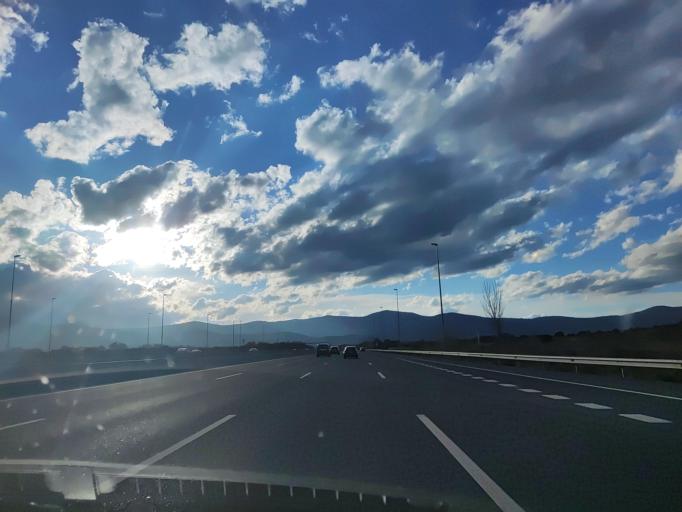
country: ES
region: Madrid
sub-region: Provincia de Madrid
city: Alpedrete
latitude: 40.6451
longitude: -4.0453
